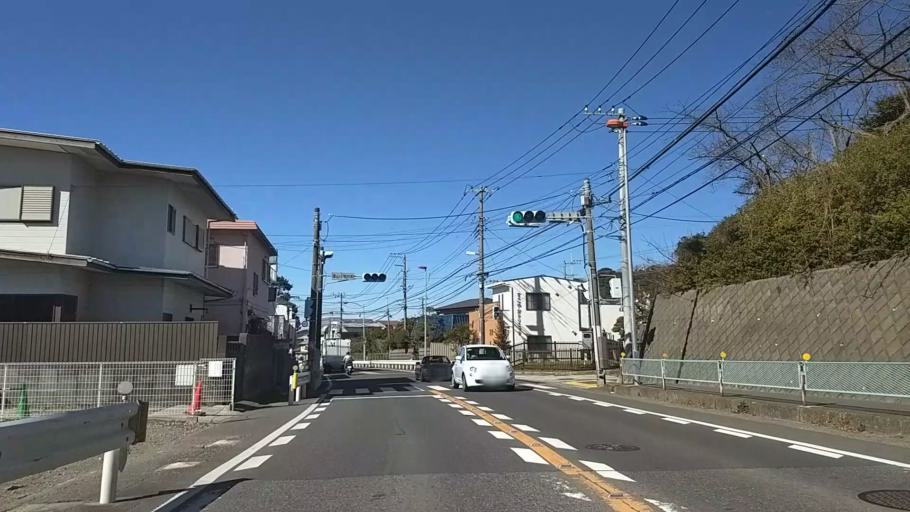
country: JP
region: Kanagawa
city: Hayama
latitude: 35.2719
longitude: 139.5832
